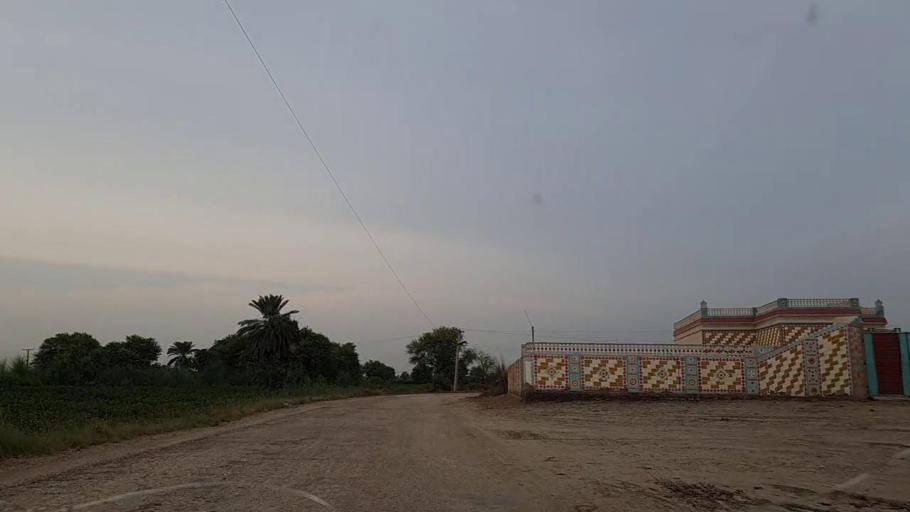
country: PK
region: Sindh
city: Mirpur Mathelo
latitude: 27.8710
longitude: 69.6344
